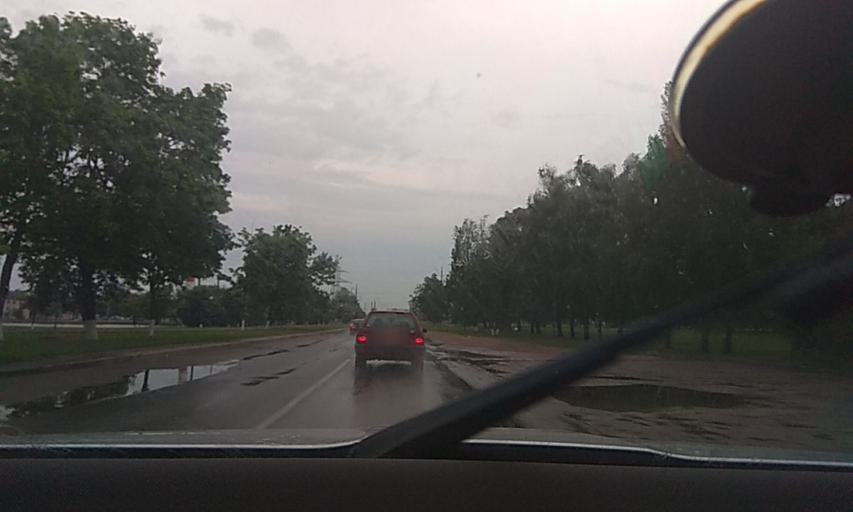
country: BY
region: Grodnenskaya
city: Hrodna
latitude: 53.6756
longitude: 23.8894
